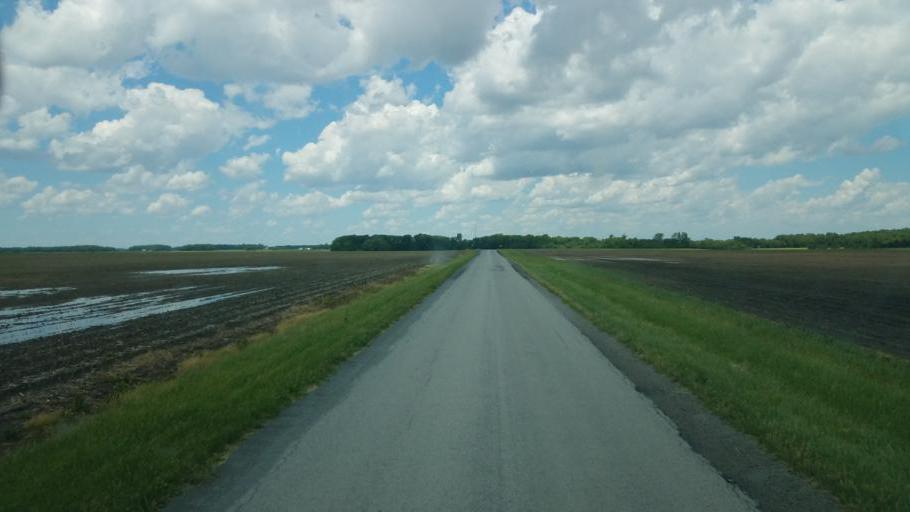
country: US
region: Ohio
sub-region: Wyandot County
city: Upper Sandusky
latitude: 40.7575
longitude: -83.2409
